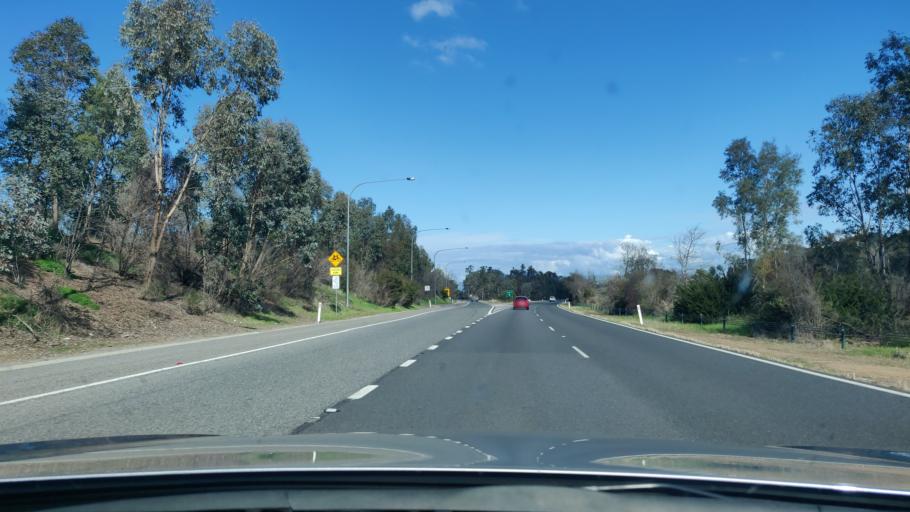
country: AU
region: New South Wales
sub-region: Albury Municipality
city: Lavington
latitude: -36.0353
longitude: 146.9757
